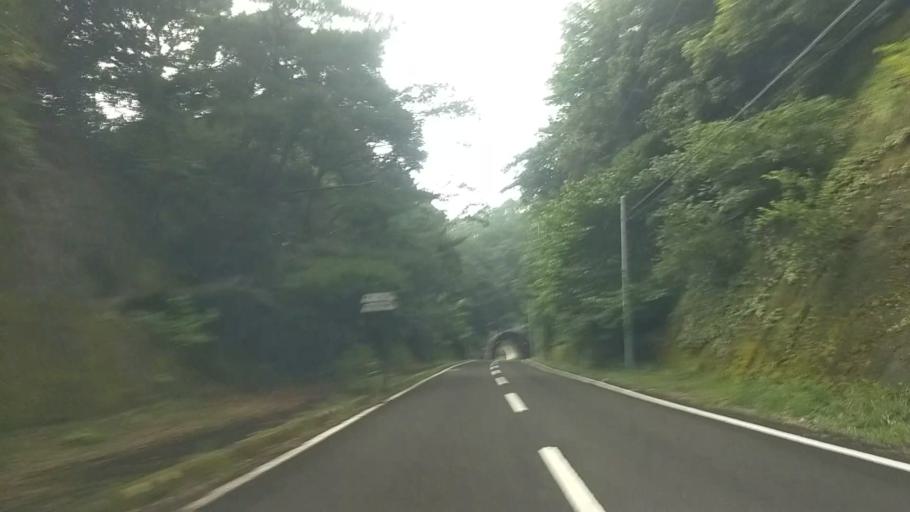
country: JP
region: Chiba
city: Kawaguchi
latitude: 35.1666
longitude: 140.1400
